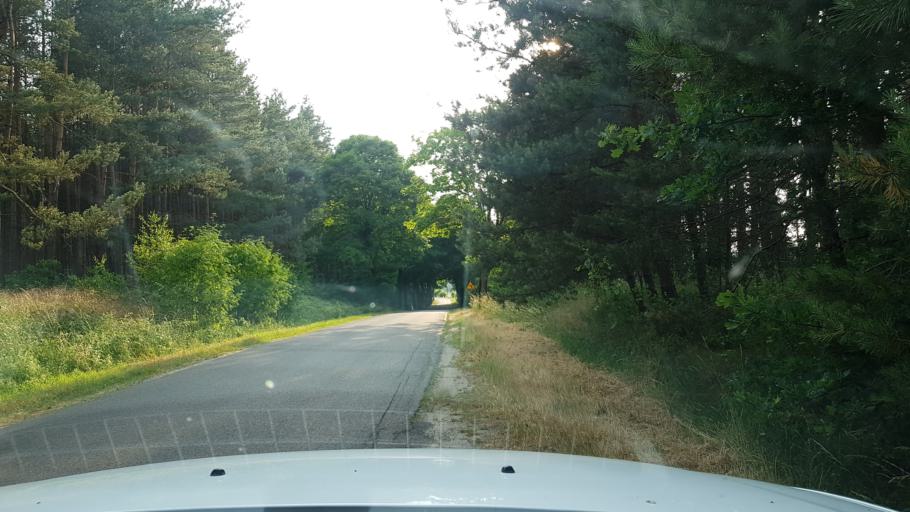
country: PL
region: West Pomeranian Voivodeship
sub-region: Powiat swidwinski
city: Swidwin
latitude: 53.8094
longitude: 15.8060
